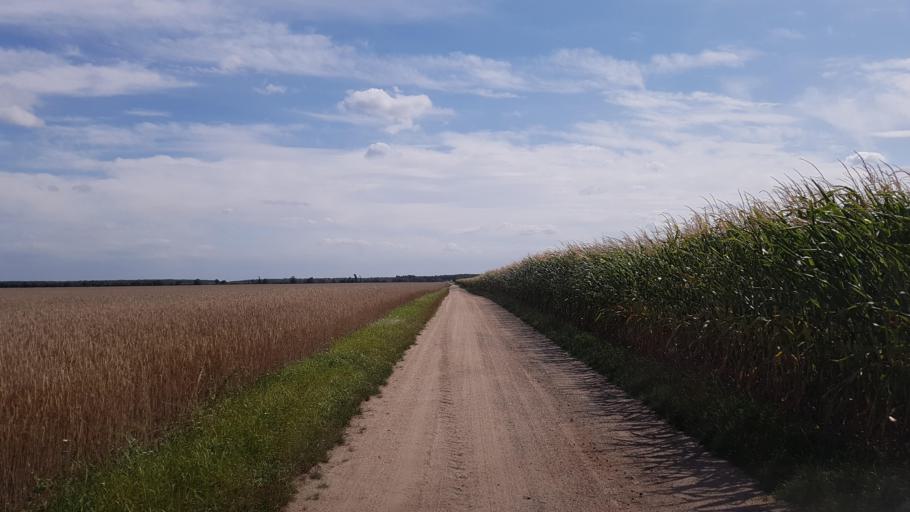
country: DE
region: Brandenburg
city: Muhlberg
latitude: 51.4654
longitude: 13.2807
